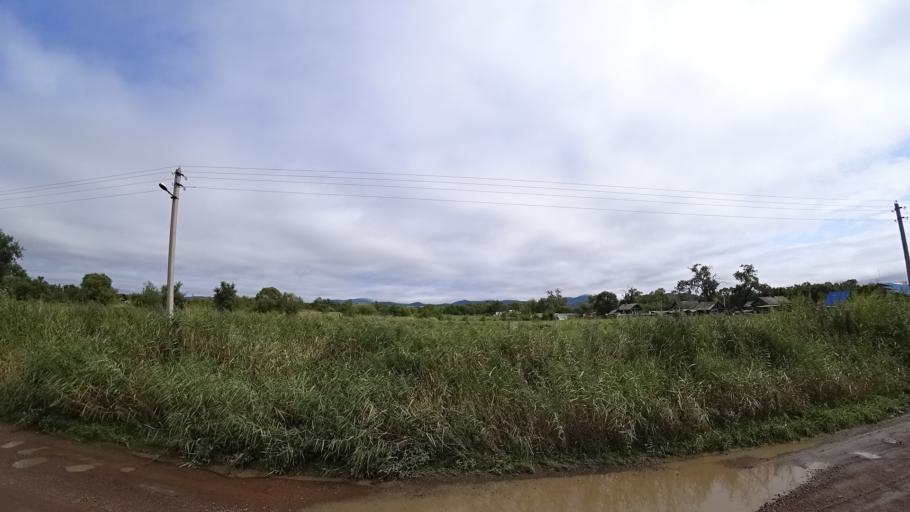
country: RU
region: Primorskiy
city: Monastyrishche
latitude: 44.1886
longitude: 132.4826
